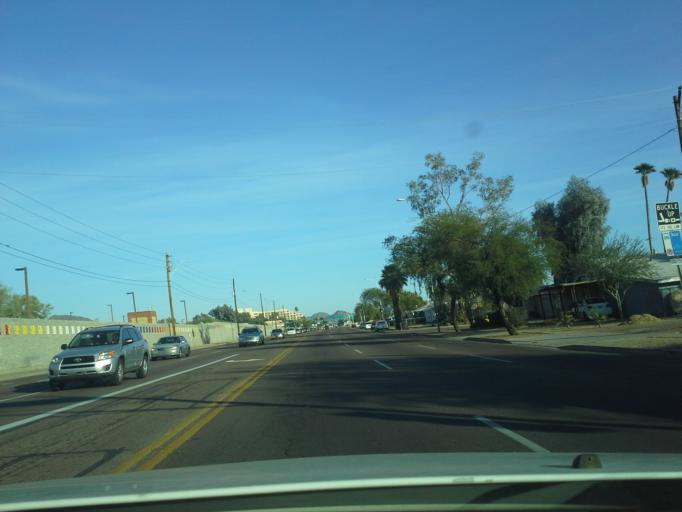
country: US
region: Arizona
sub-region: Maricopa County
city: Glendale
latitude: 33.5675
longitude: -112.1254
